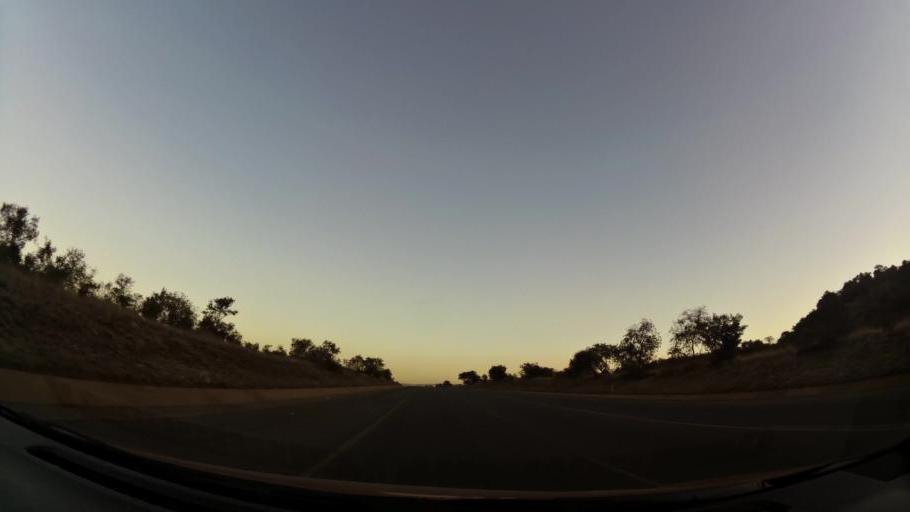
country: ZA
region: North-West
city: Ga-Rankuwa
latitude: -25.6059
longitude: 28.0391
